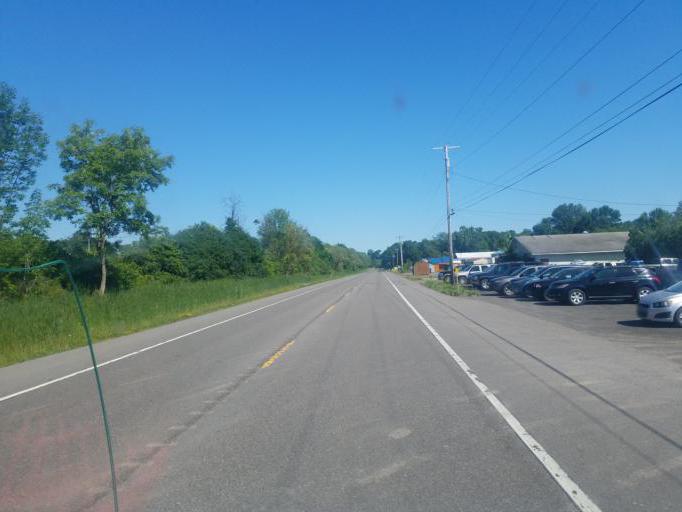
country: US
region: New York
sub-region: Wayne County
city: Lyons
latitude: 43.0637
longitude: -77.0237
